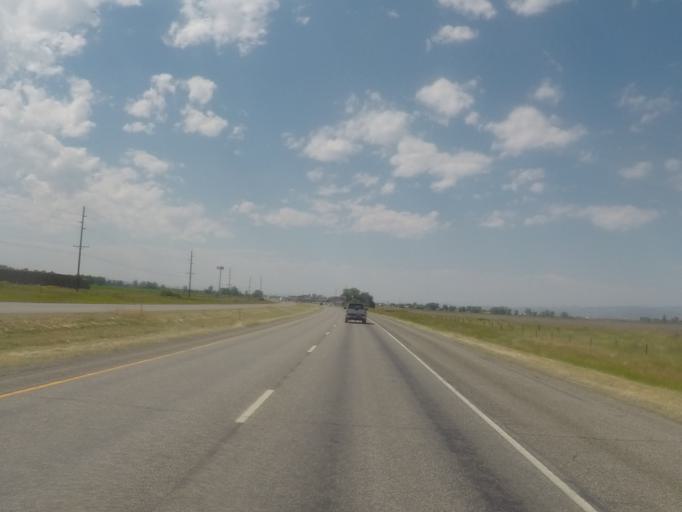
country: US
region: Montana
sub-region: Gallatin County
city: Belgrade
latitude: 45.7443
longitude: -111.1182
